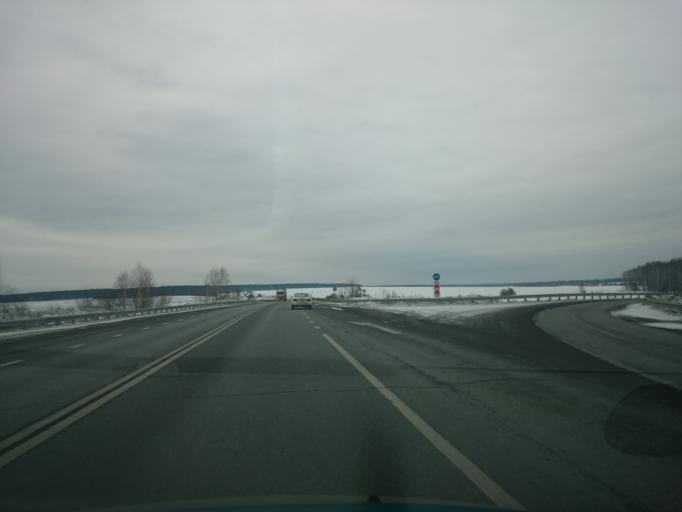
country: RU
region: Sverdlovsk
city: Achit
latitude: 56.7896
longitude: 57.8811
